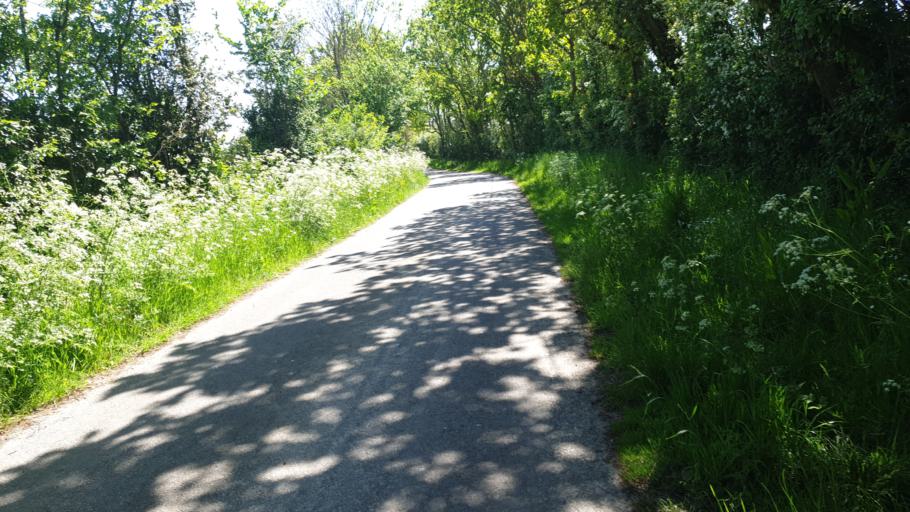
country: GB
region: England
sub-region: Essex
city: Great Bentley
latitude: 51.8910
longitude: 1.0384
